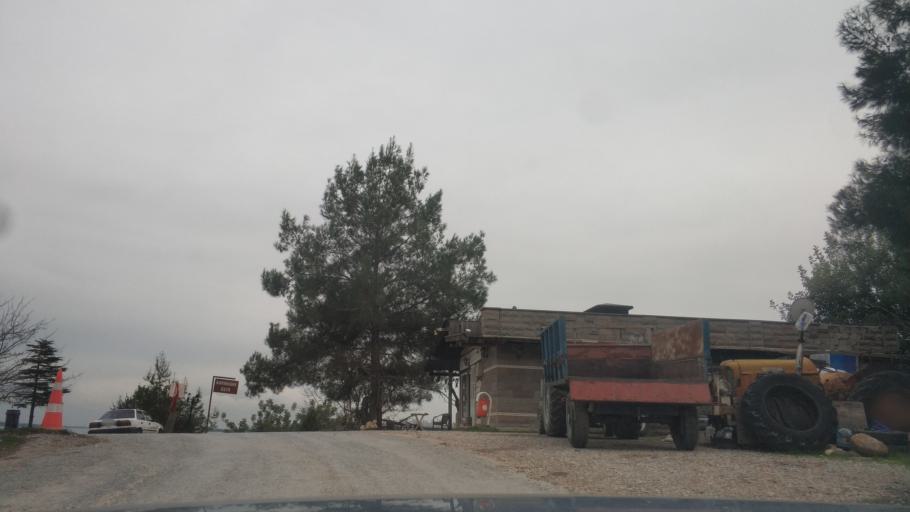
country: TR
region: Adana
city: Adana
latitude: 37.0968
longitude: 35.2824
